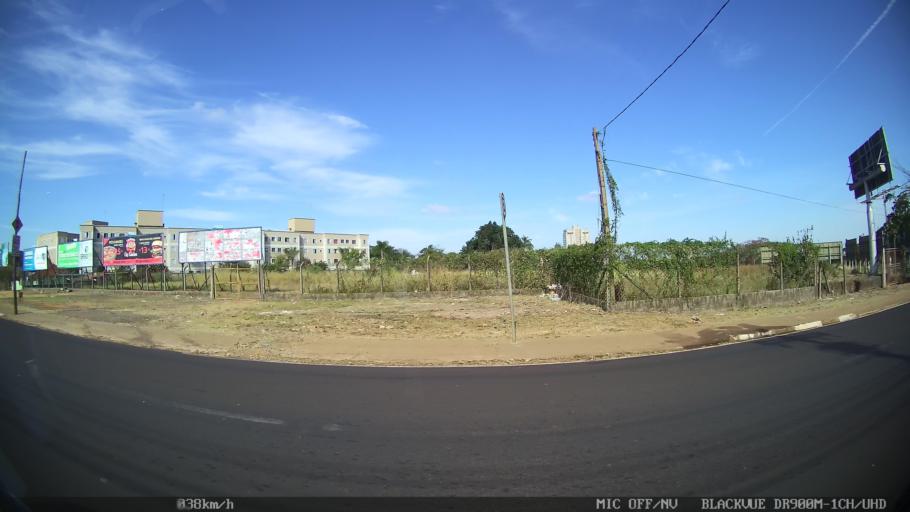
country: BR
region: Sao Paulo
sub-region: Franca
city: Franca
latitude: -20.5427
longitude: -47.4211
